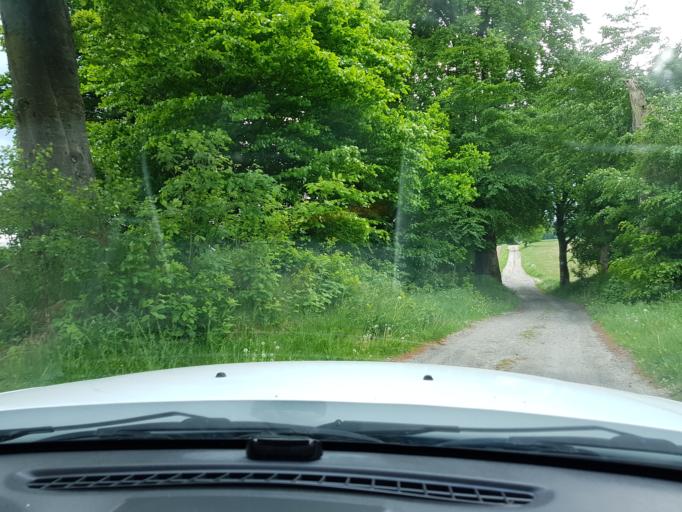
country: PL
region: West Pomeranian Voivodeship
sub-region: Powiat drawski
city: Drawsko Pomorskie
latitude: 53.5418
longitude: 15.7365
